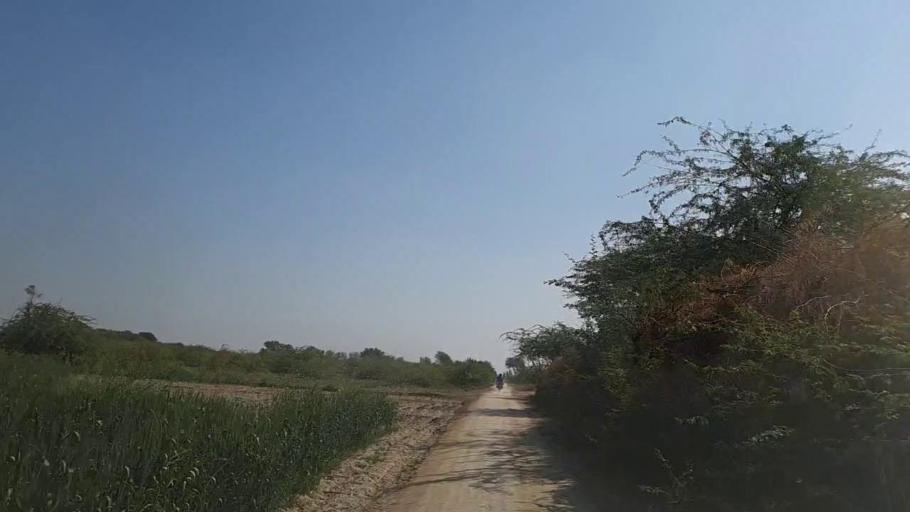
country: PK
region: Sindh
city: Digri
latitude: 25.1657
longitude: 69.1728
